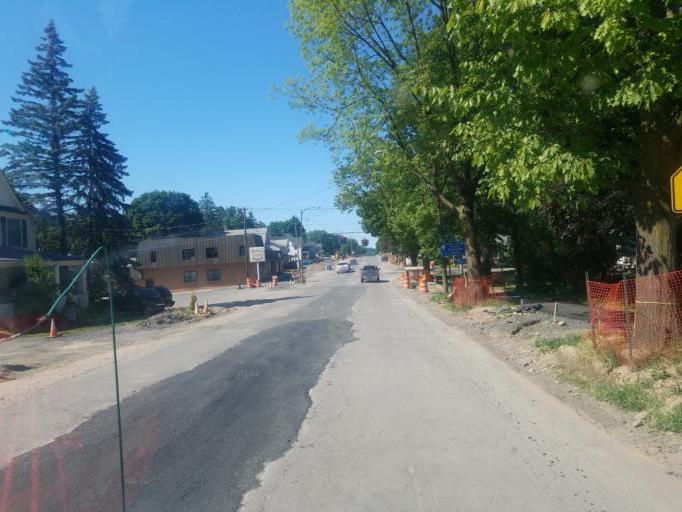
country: US
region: New York
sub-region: Wayne County
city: Newark
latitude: 43.0389
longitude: -77.0961
